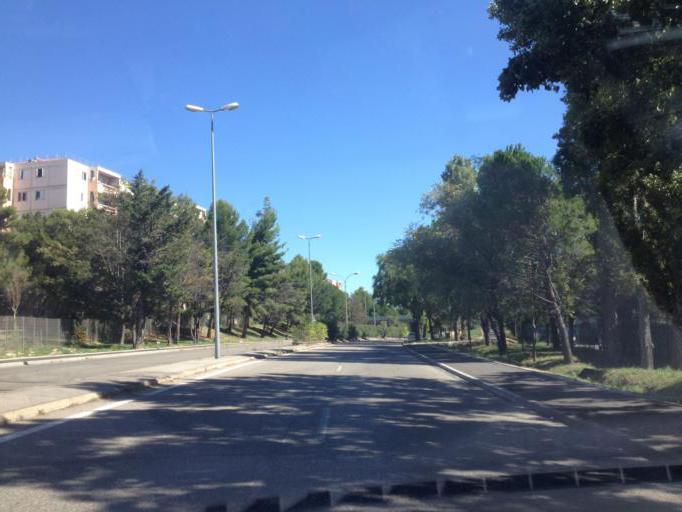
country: FR
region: Provence-Alpes-Cote d'Azur
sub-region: Departement des Bouches-du-Rhone
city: Aix-en-Provence
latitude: 43.5303
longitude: 5.4109
